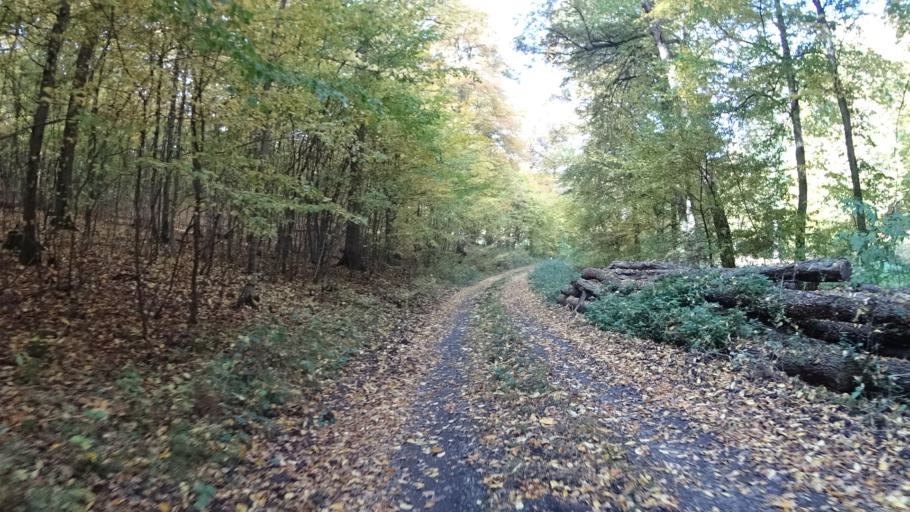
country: DE
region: Rheinland-Pfalz
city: Stein-Bockenheim
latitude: 49.7550
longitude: 7.9635
